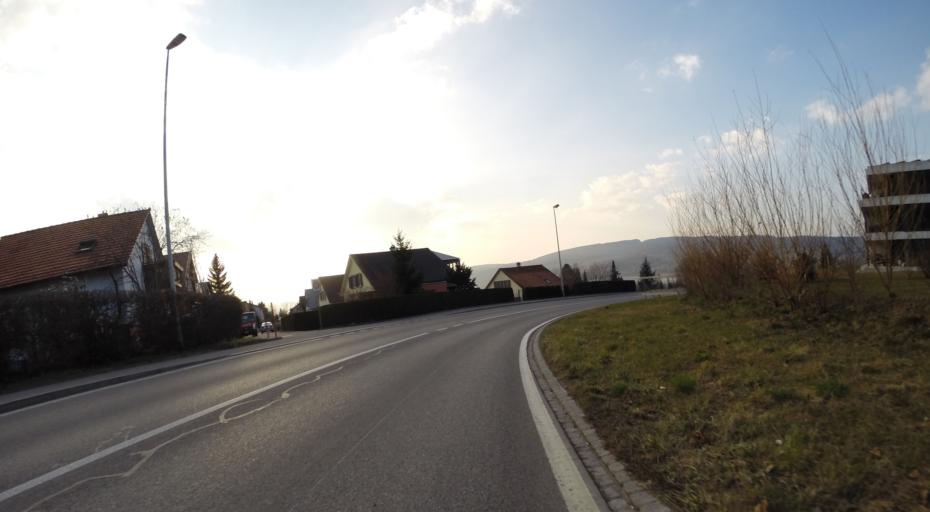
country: CH
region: Thurgau
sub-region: Frauenfeld District
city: Steckborn
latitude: 47.6593
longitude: 8.9814
